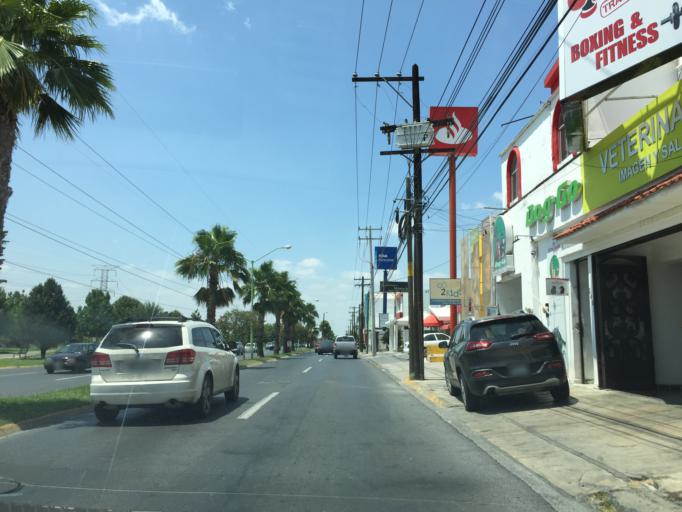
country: MX
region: Nuevo Leon
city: Guadalupe
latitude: 25.6430
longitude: -100.2685
